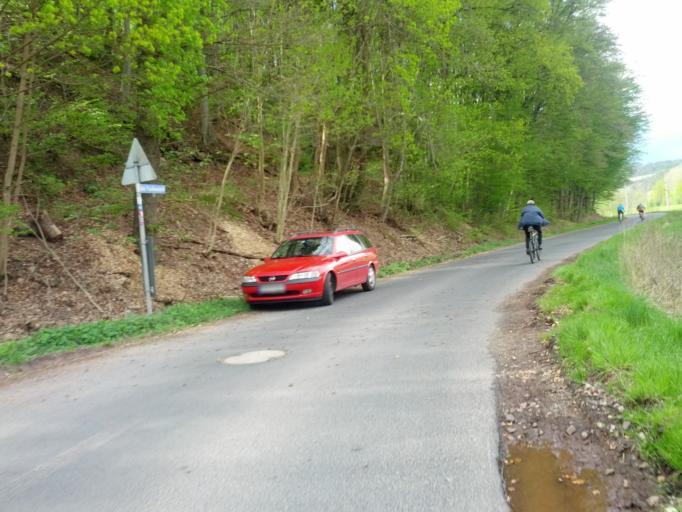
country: DE
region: Thuringia
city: Krauthausen
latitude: 50.9893
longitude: 10.2493
